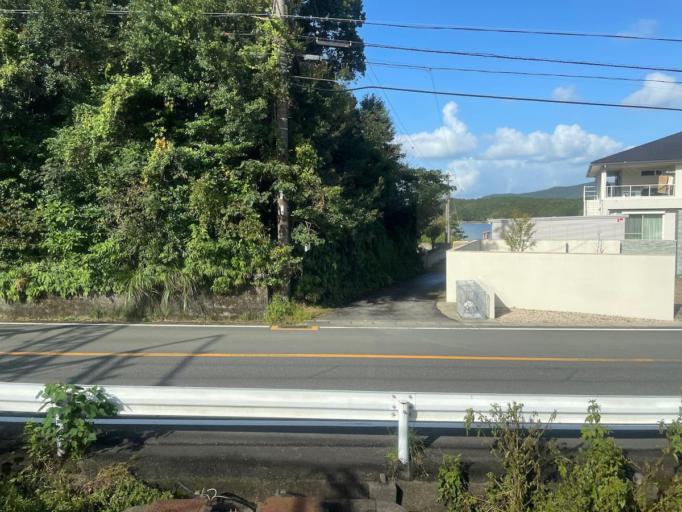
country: JP
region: Mie
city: Toba
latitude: 34.3124
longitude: 136.8253
